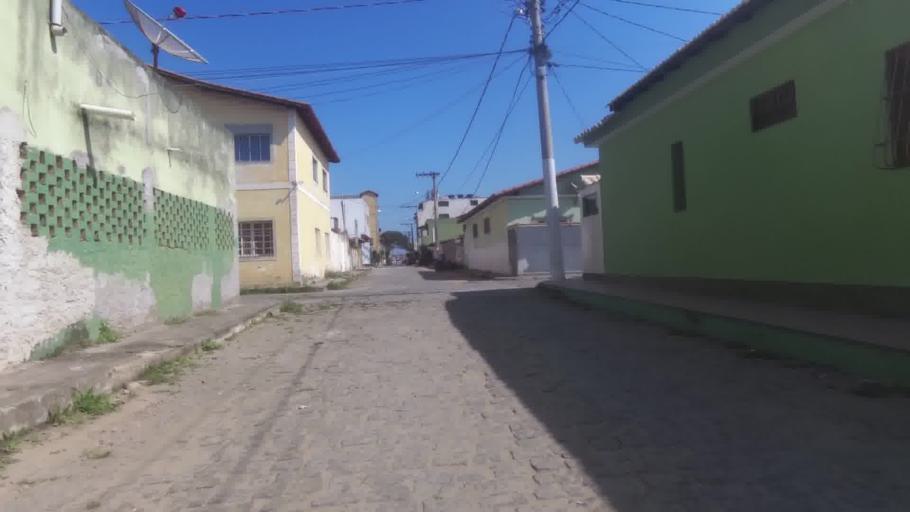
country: BR
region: Espirito Santo
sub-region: Itapemirim
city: Itapemirim
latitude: -21.0099
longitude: -40.8087
